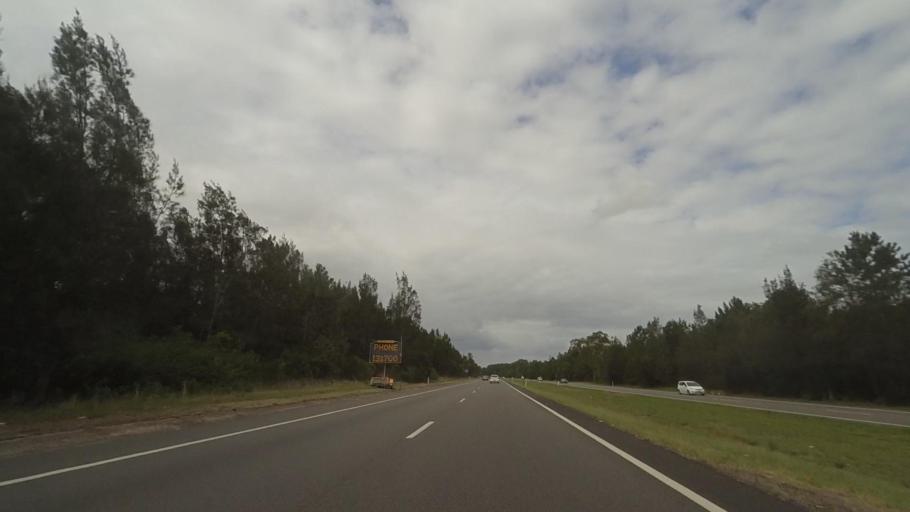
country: AU
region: New South Wales
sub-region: Port Stephens Shire
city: Raymond Terrace
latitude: -32.7741
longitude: 151.7575
